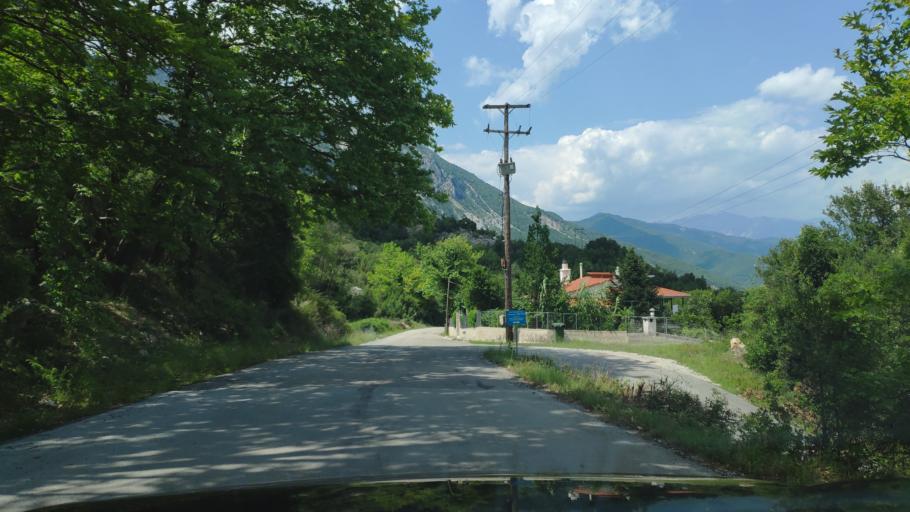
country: GR
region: Epirus
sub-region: Nomos Artas
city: Agios Dimitrios
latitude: 39.4264
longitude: 21.0158
